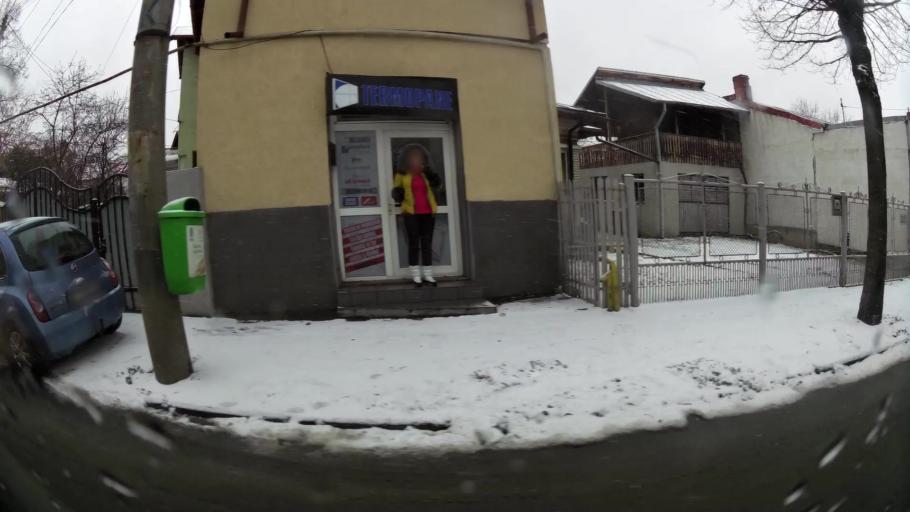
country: RO
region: Prahova
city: Ploiesti
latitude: 44.9385
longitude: 26.0142
